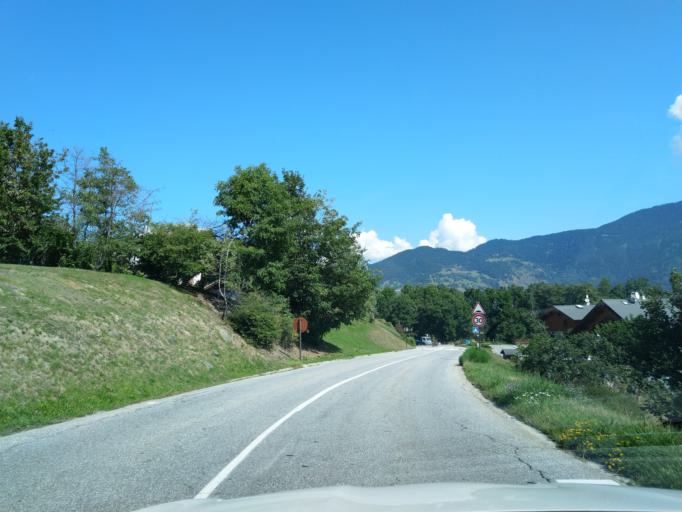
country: FR
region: Rhone-Alpes
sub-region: Departement de la Savoie
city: Les Allues
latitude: 45.4342
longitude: 6.5556
